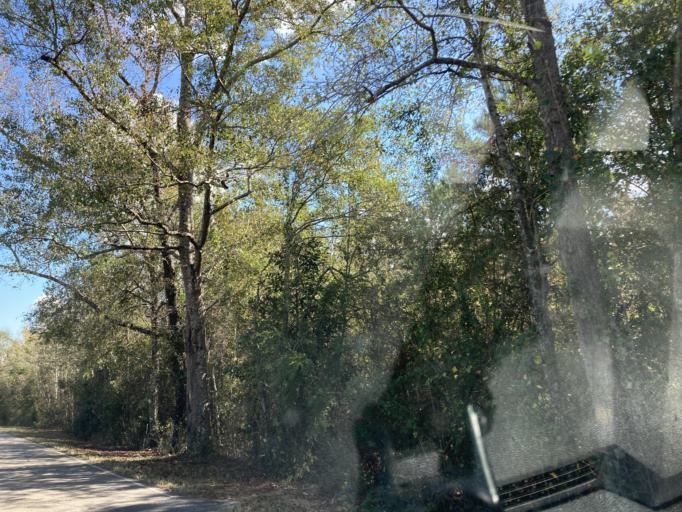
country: US
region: Mississippi
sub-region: Lamar County
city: Purvis
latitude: 31.2295
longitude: -89.4229
